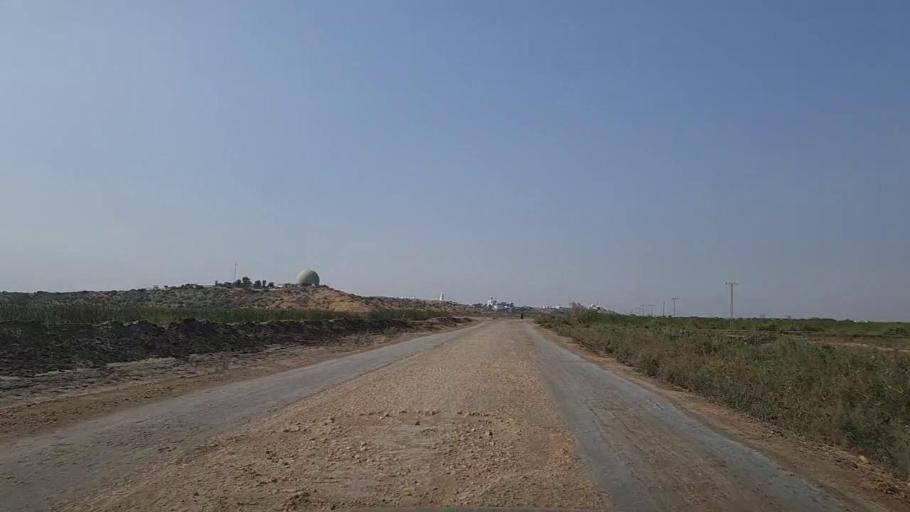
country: PK
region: Sindh
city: Chuhar Jamali
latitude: 24.5508
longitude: 67.8939
